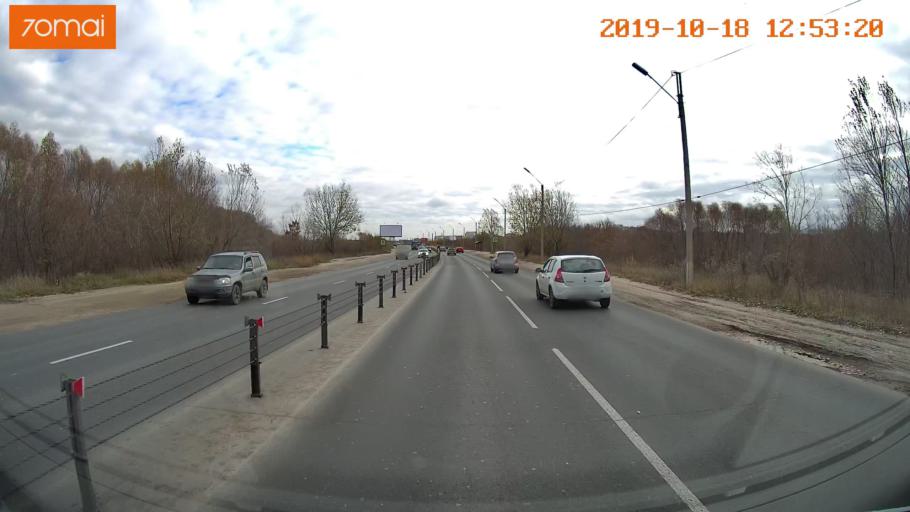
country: RU
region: Rjazan
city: Ryazan'
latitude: 54.6451
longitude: 39.7052
